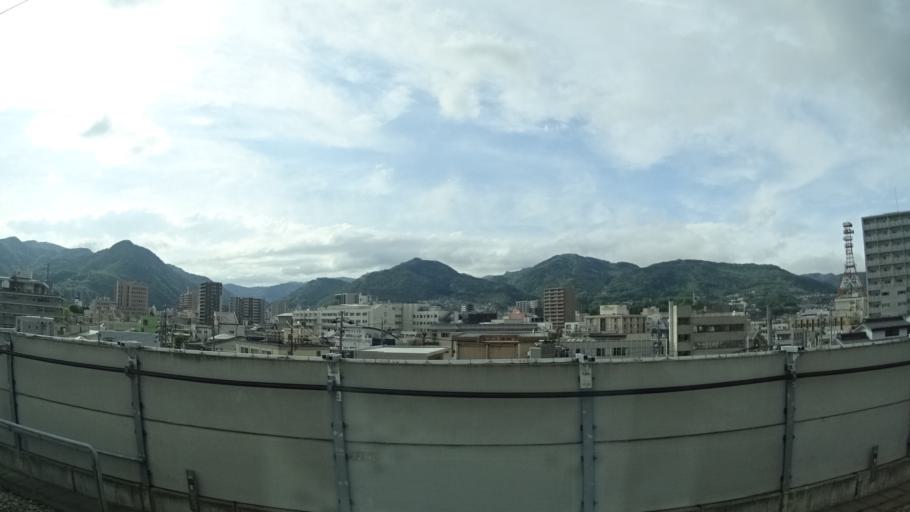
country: JP
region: Nagano
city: Nagano-shi
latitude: 36.6500
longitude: 138.1986
